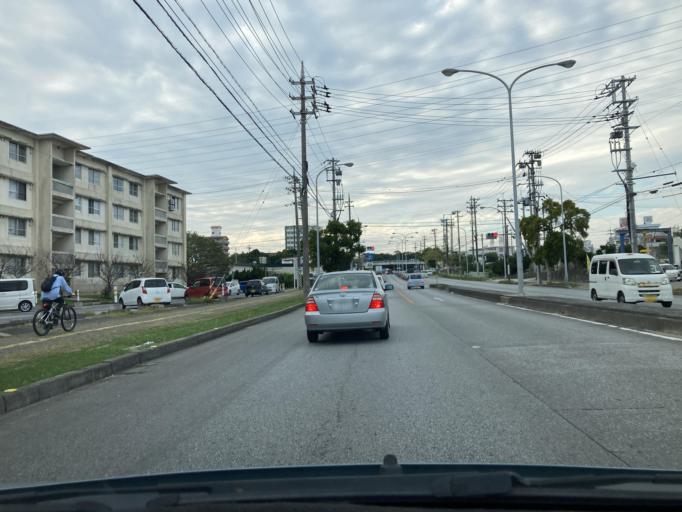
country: JP
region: Okinawa
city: Okinawa
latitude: 26.3537
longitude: 127.8076
